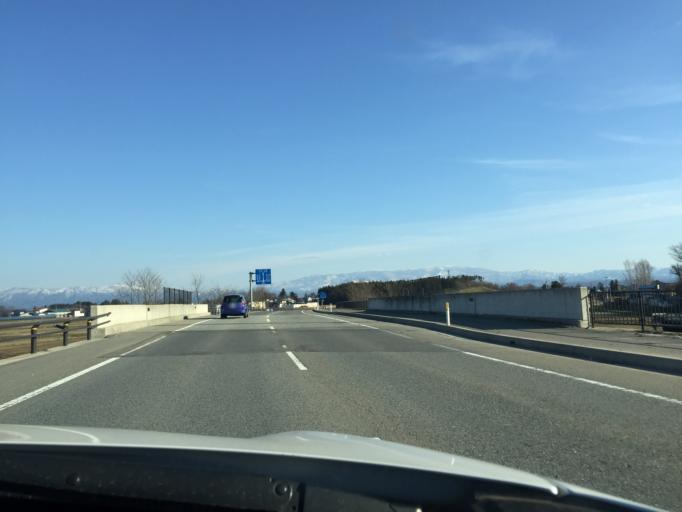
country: JP
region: Yamagata
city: Nagai
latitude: 38.0551
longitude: 140.0604
